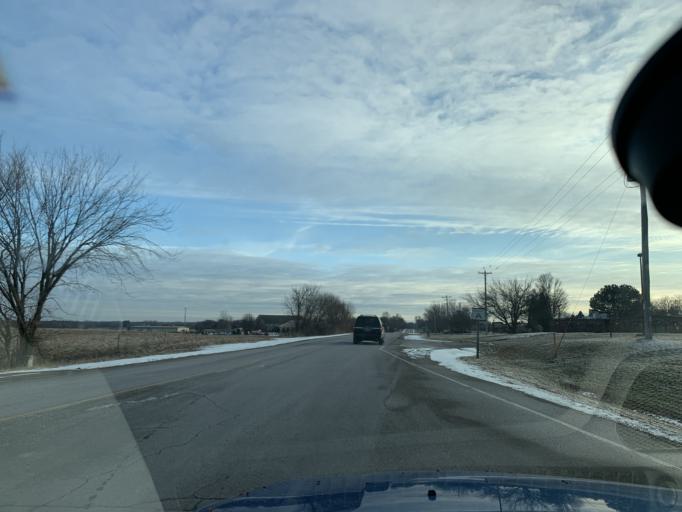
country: US
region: Wisconsin
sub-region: Rock County
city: Edgerton
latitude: 42.9208
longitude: -89.0918
